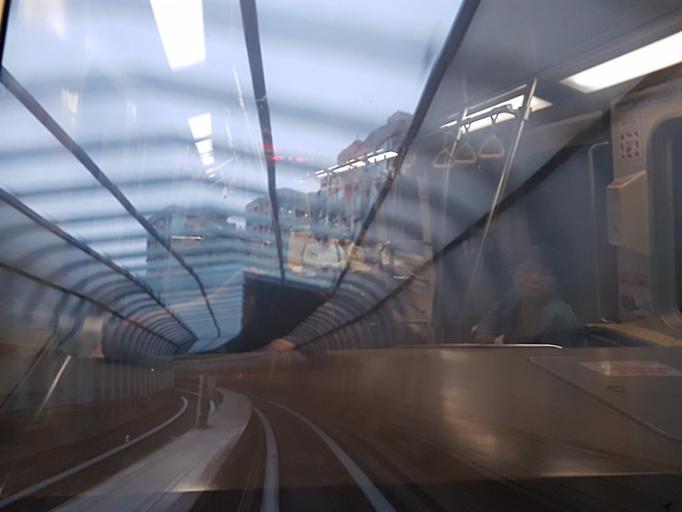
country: TW
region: Taipei
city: Taipei
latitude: 25.0748
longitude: 121.6068
